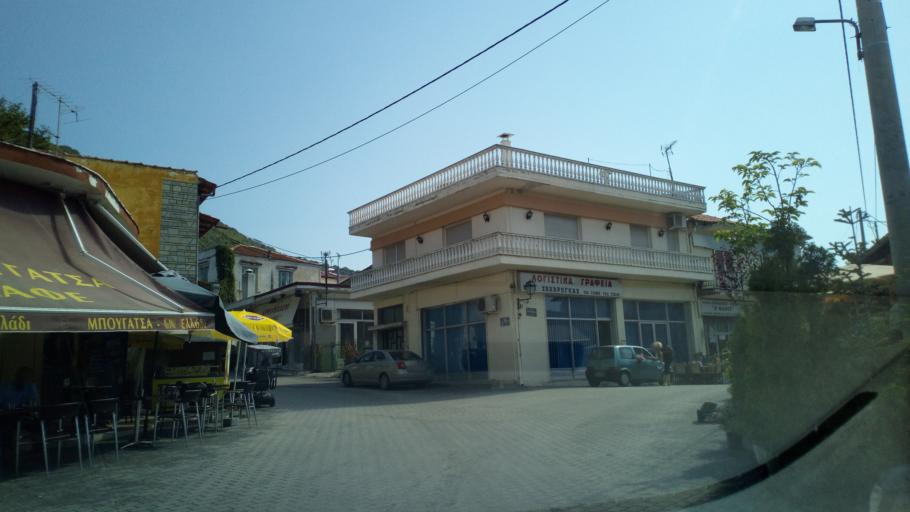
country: GR
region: Central Macedonia
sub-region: Nomos Thessalonikis
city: Sochos
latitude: 40.8174
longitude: 23.3548
